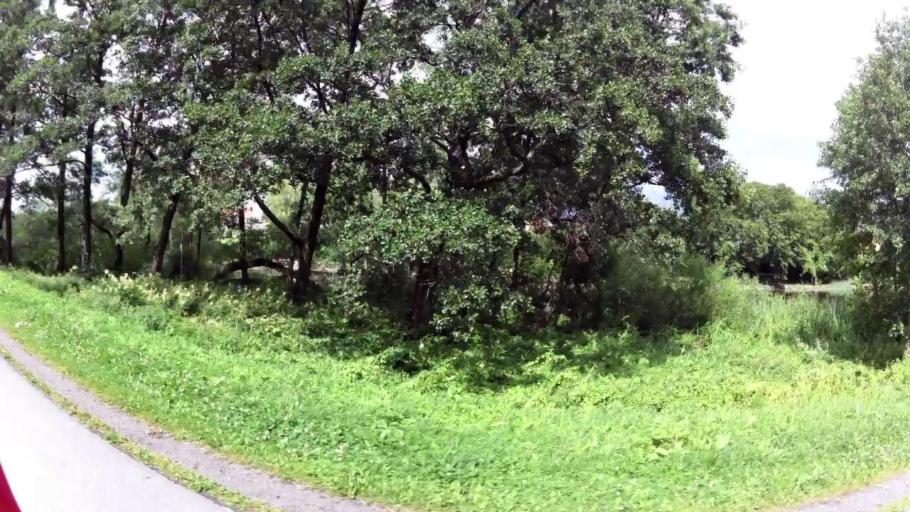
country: SE
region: OEstergoetland
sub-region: Linkopings Kommun
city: Linkoping
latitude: 58.4043
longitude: 15.6382
